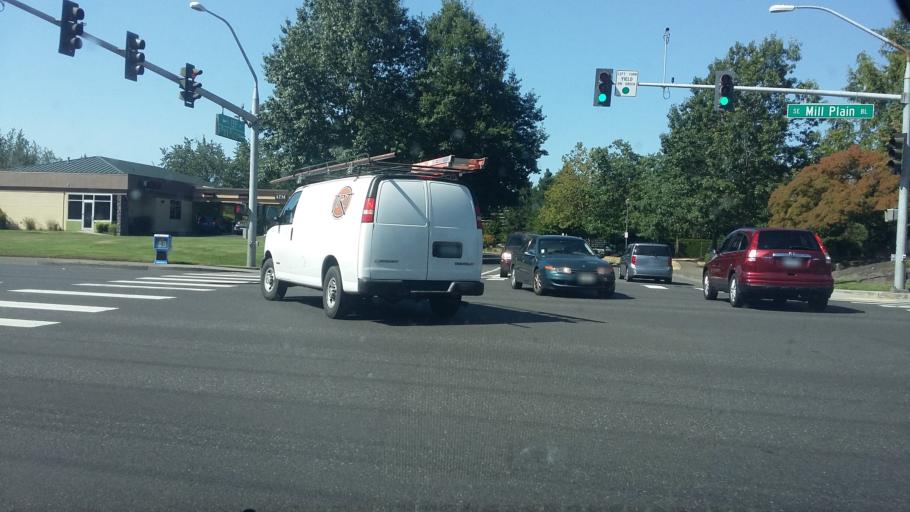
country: US
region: Washington
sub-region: Clark County
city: Mill Plain
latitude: 45.6191
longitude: -122.5380
